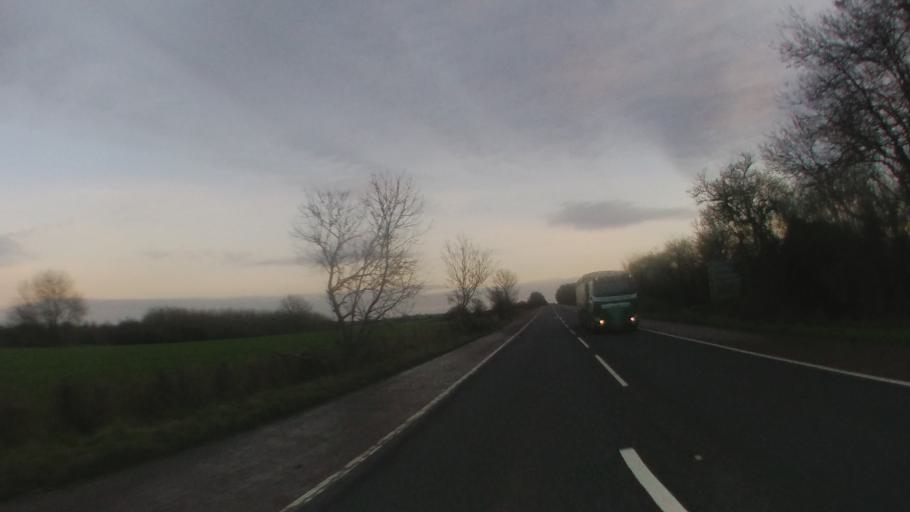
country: GB
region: Northern Ireland
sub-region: Armagh District
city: Tandragee
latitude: 54.2883
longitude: -6.4977
